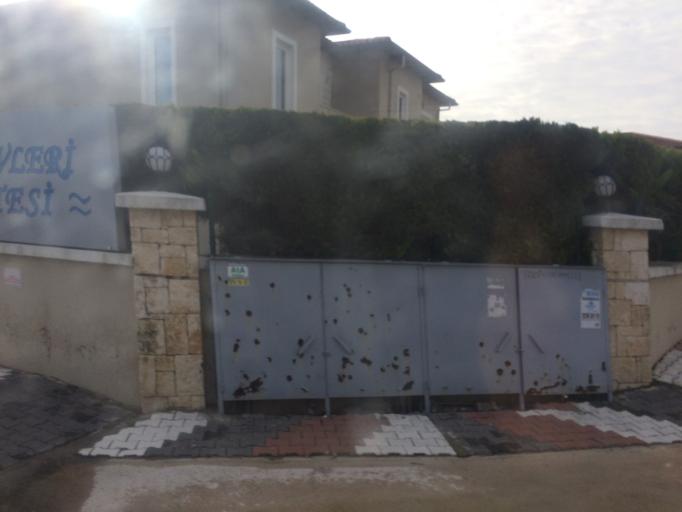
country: TR
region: Izmir
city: Menemen
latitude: 38.5015
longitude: 26.9597
